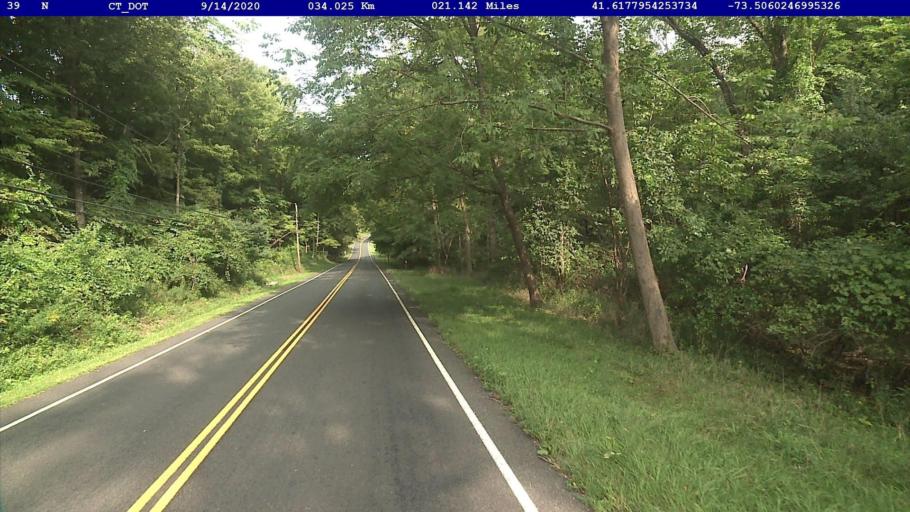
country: US
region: Connecticut
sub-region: Fairfield County
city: Sherman
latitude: 41.6178
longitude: -73.5062
